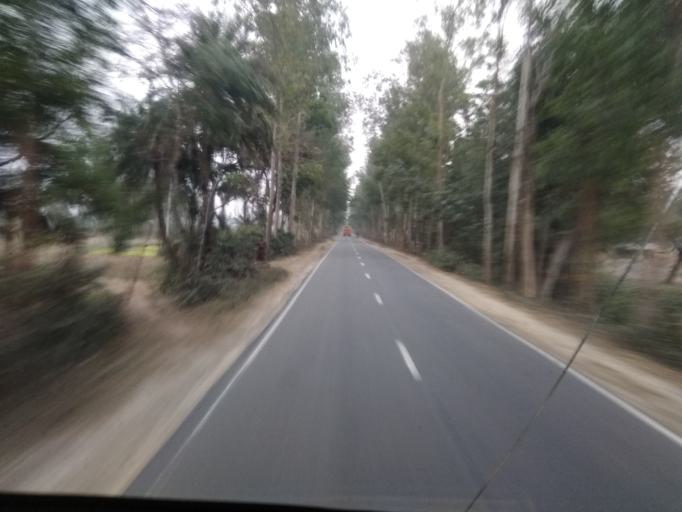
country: BD
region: Rajshahi
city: Bogra
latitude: 24.6830
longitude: 89.2893
